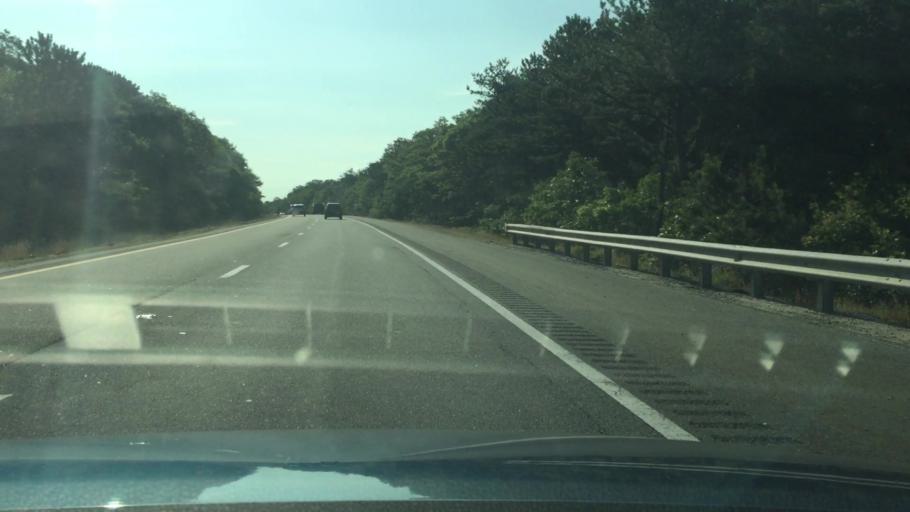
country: US
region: Massachusetts
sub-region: Barnstable County
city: Barnstable
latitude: 41.6869
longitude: -70.2996
